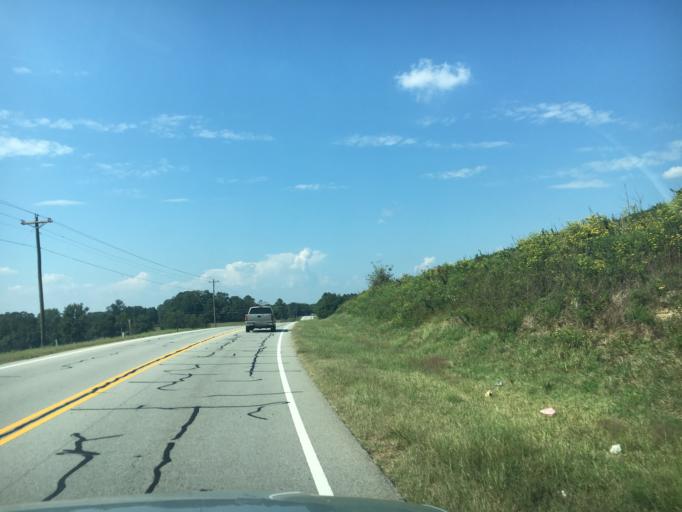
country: US
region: Georgia
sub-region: Franklin County
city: Lavonia
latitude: 34.4325
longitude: -83.0302
